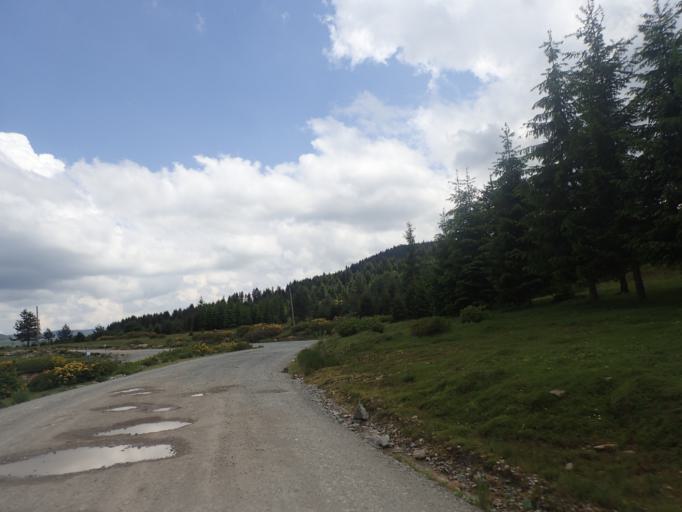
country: TR
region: Ordu
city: Topcam
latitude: 40.6828
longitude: 37.9379
